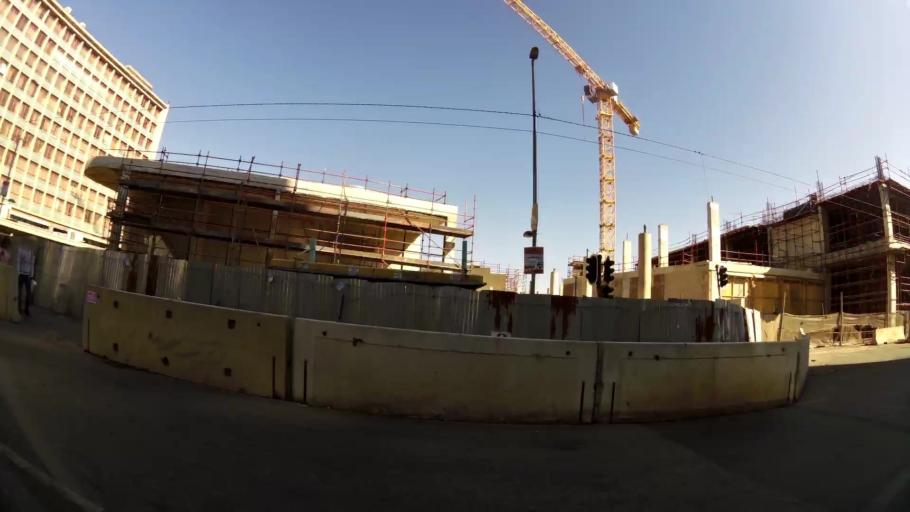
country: ZA
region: Gauteng
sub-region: City of Johannesburg Metropolitan Municipality
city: Johannesburg
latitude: -26.1997
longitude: 28.0395
